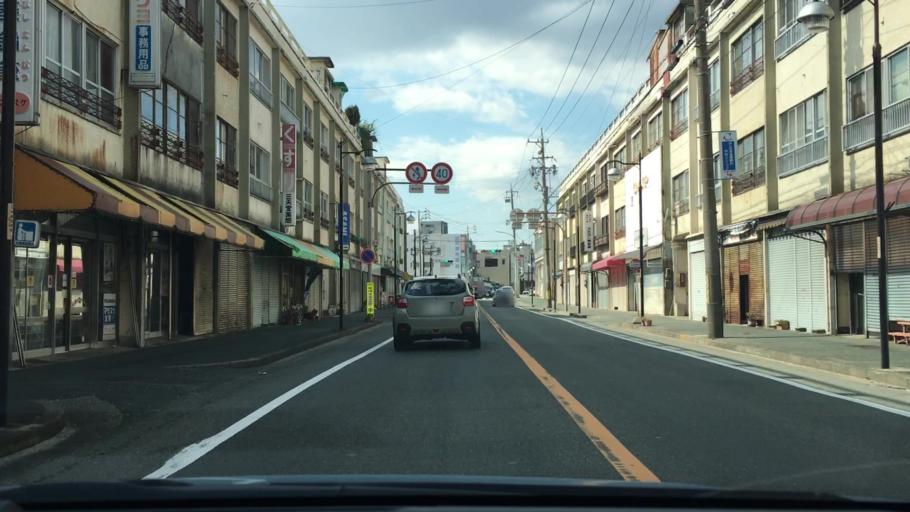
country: JP
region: Aichi
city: Gamagori
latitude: 34.8128
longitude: 137.2504
